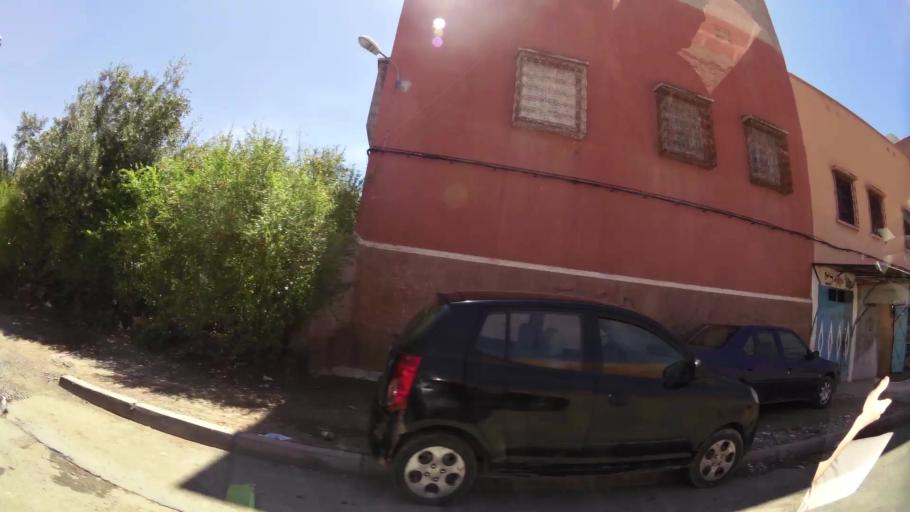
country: MA
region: Marrakech-Tensift-Al Haouz
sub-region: Marrakech
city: Marrakesh
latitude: 31.6323
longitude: -8.0456
